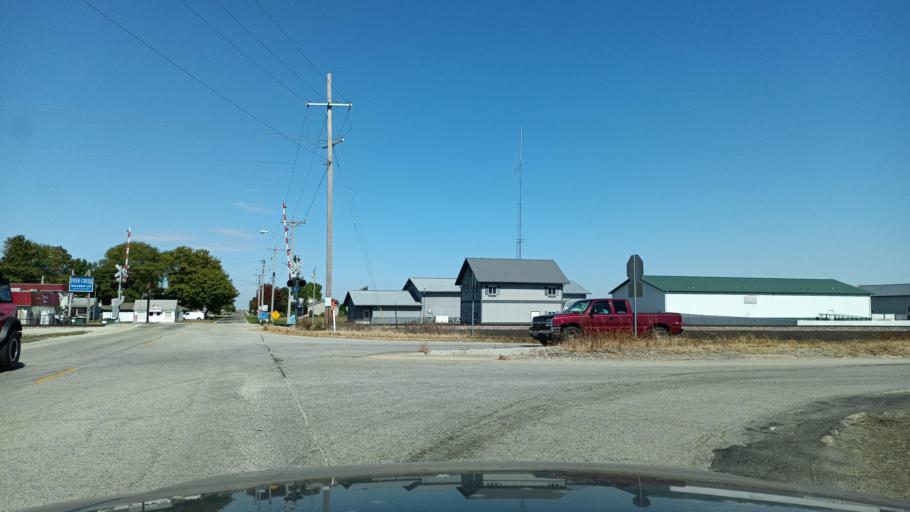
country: US
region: Illinois
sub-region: Tazewell County
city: Mackinaw
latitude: 40.6266
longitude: -89.3278
